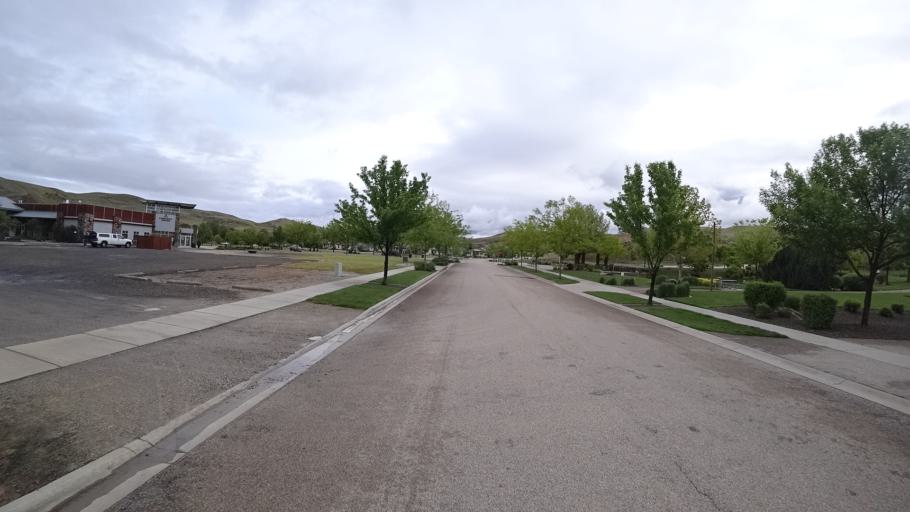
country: US
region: Idaho
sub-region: Ada County
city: Eagle
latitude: 43.7722
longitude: -116.2620
